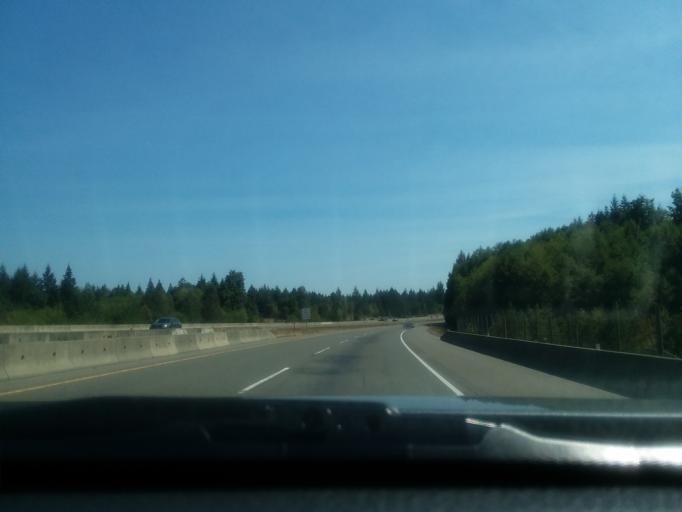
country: CA
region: British Columbia
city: Port Alberni
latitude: 49.4850
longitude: -124.8143
